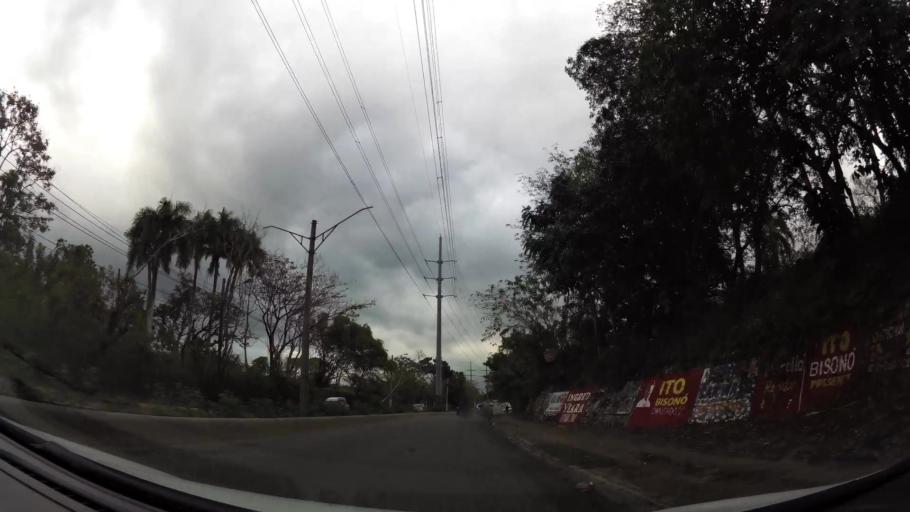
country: DO
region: Nacional
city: Santo Domingo
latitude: 18.5070
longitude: -69.9732
